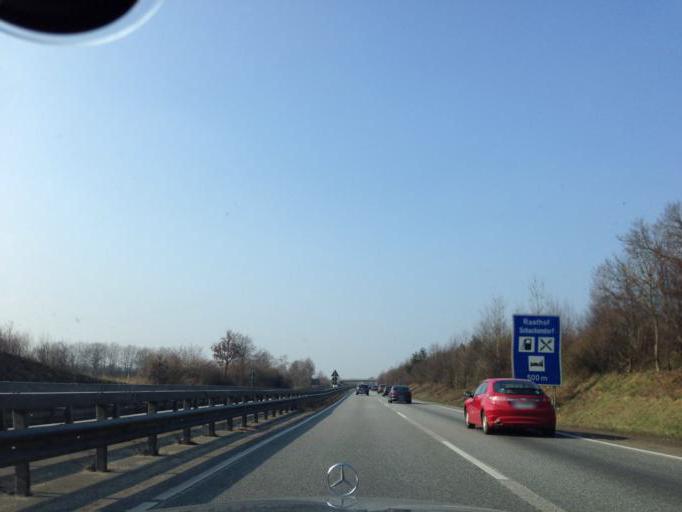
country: DE
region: Schleswig-Holstein
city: Schackendorf
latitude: 53.9540
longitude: 10.2706
